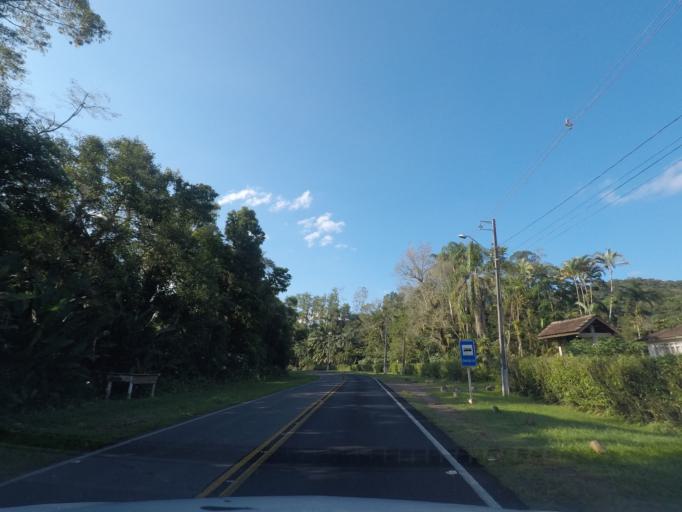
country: BR
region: Parana
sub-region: Antonina
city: Antonina
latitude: -25.4191
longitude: -48.8743
